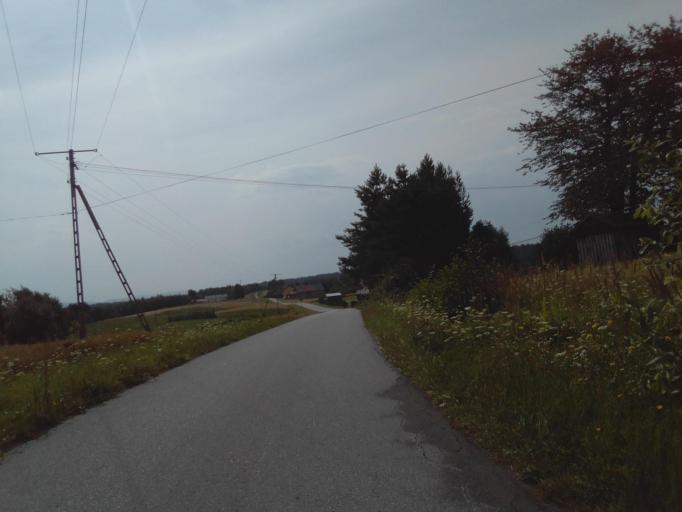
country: PL
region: Subcarpathian Voivodeship
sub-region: Powiat strzyzowski
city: Frysztak
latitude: 49.8676
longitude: 21.5280
